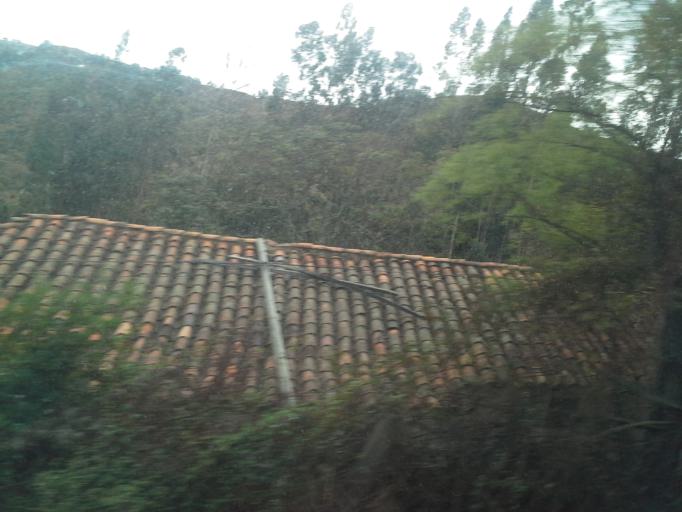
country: CO
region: Boyaca
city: Raquira
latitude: 5.5450
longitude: -73.6365
